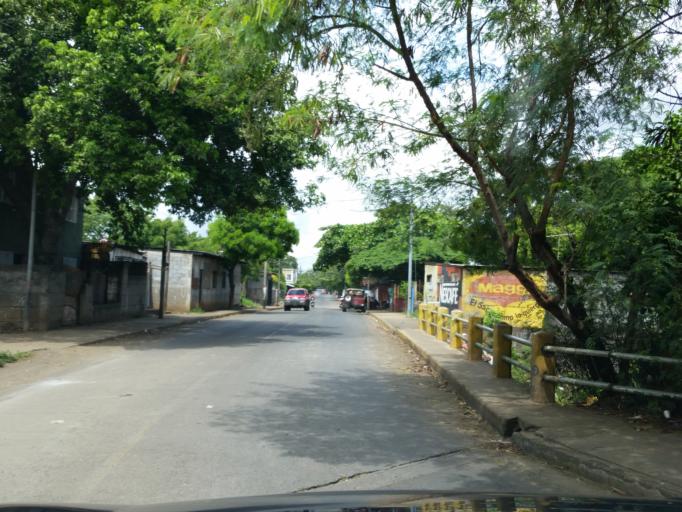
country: NI
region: Managua
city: Managua
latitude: 12.1344
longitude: -86.2502
